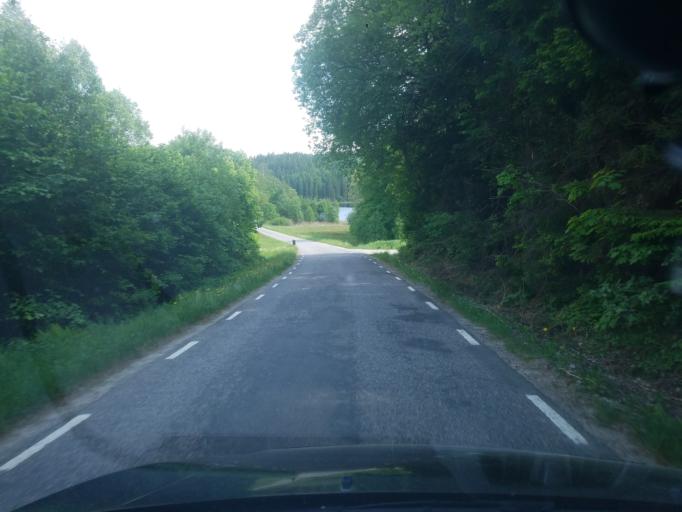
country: SE
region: Vaestra Goetaland
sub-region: Stenungsunds Kommun
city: Stora Hoga
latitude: 57.9992
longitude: 11.9331
